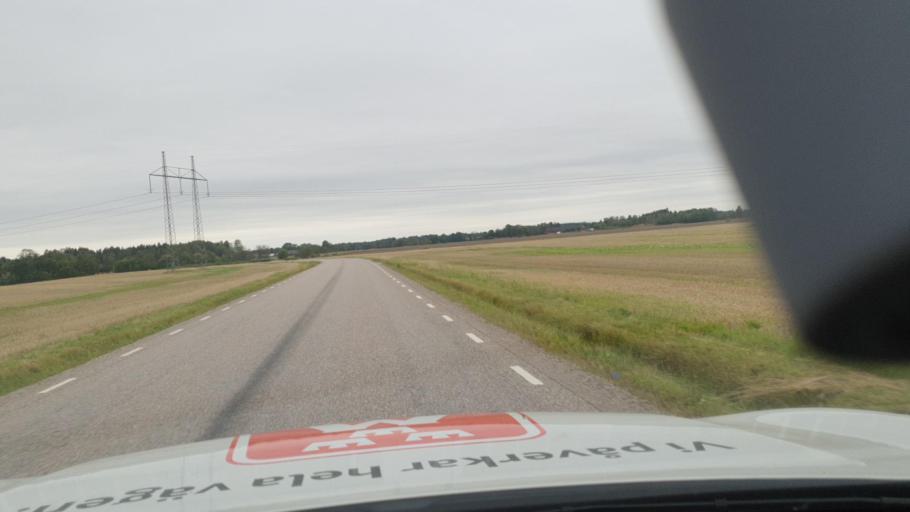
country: SE
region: Vaestra Goetaland
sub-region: Vanersborgs Kommun
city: Vanersborg
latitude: 58.4954
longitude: 12.2276
